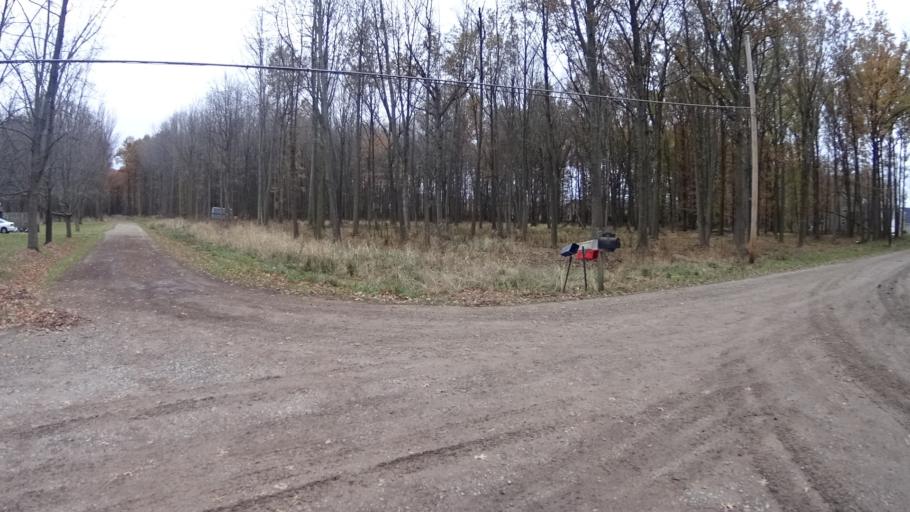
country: US
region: Ohio
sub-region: Lorain County
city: Avon Center
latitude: 41.4828
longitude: -82.0129
